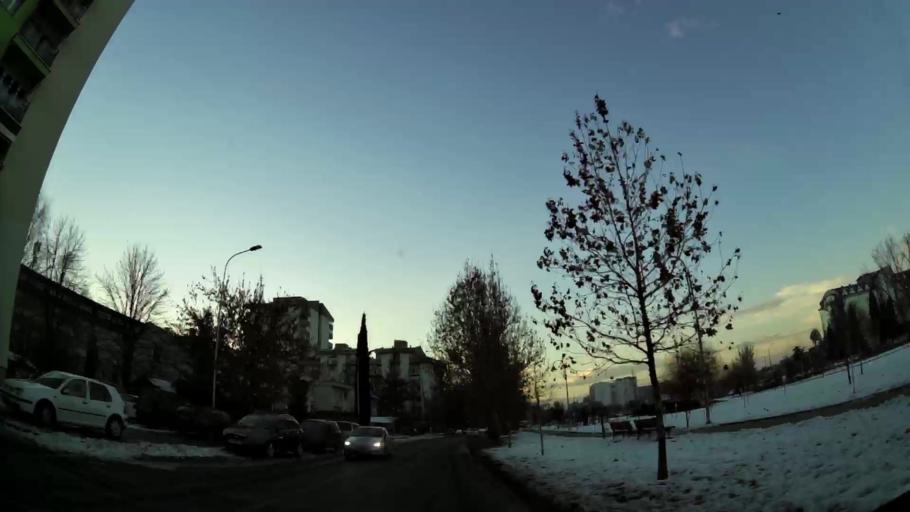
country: MK
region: Karpos
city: Skopje
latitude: 41.9956
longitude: 21.4053
